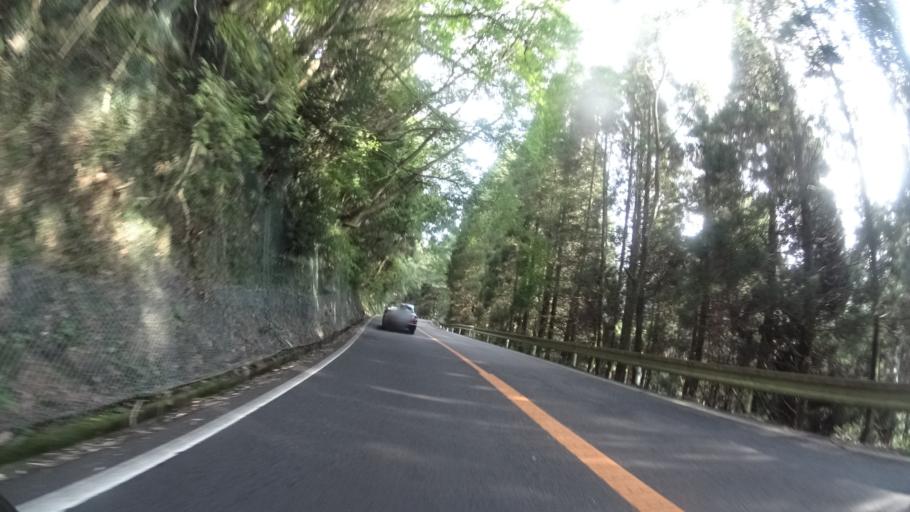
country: JP
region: Oita
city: Beppu
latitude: 33.2644
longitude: 131.3722
